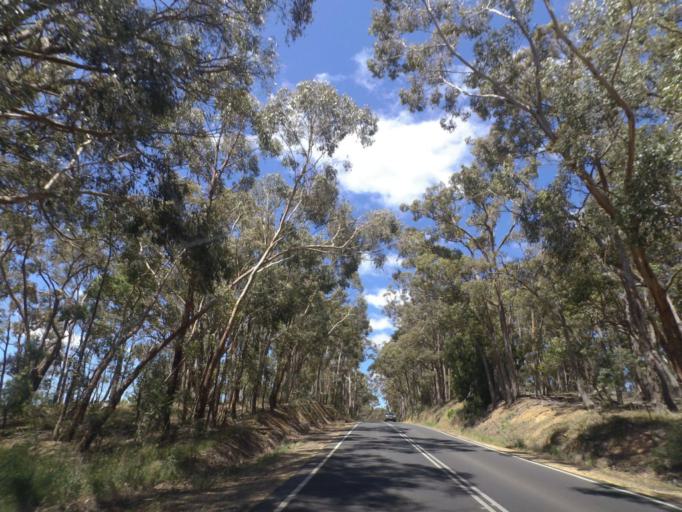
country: AU
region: Victoria
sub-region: Mount Alexander
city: Castlemaine
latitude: -37.2878
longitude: 144.2751
